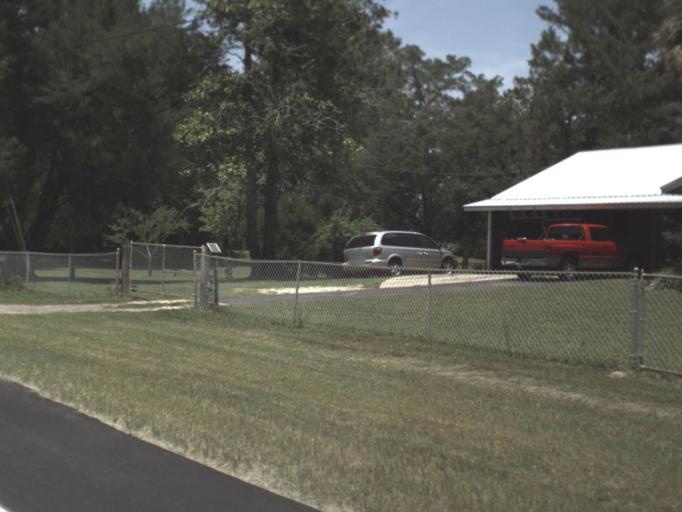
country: US
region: Florida
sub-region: Gilchrist County
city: Trenton
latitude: 29.6064
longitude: -82.8183
